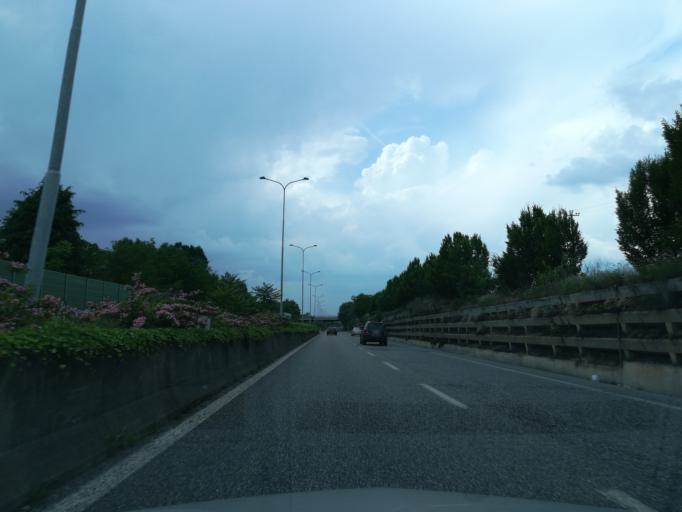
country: IT
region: Lombardy
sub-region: Provincia di Bergamo
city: Seriate
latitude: 45.6740
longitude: 9.7156
